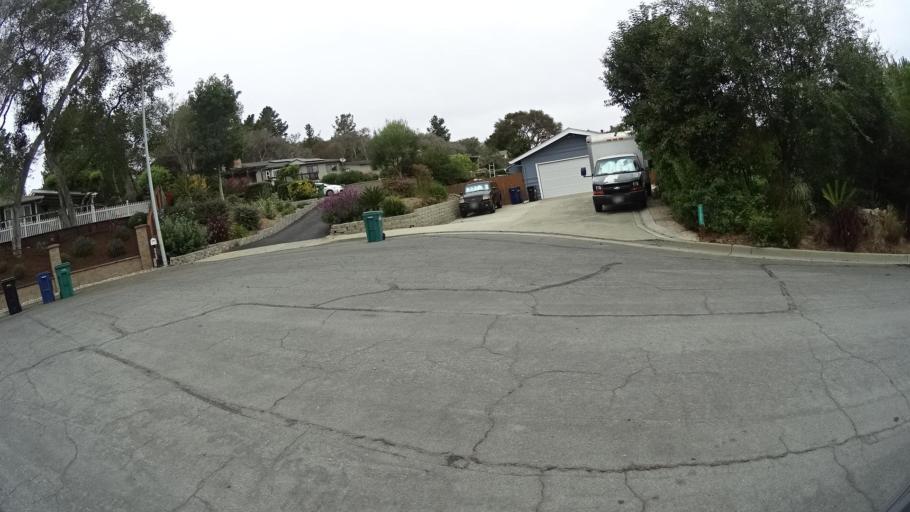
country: US
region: California
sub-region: Monterey County
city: Prunedale
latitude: 36.7776
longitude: -121.6740
